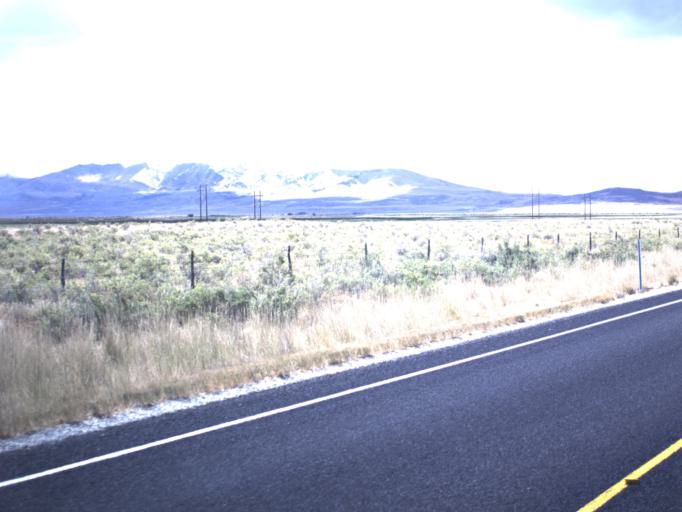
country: US
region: Utah
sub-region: Box Elder County
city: Tremonton
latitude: 41.6265
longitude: -112.3974
